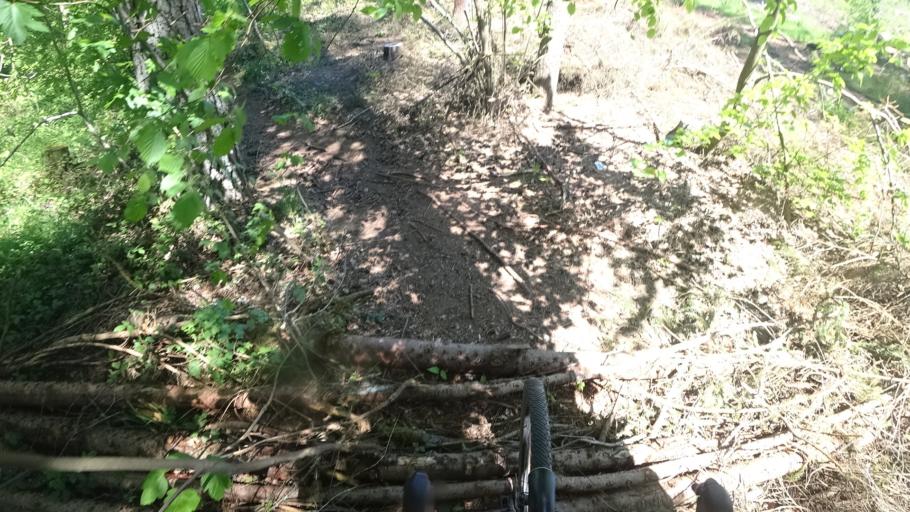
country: DE
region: Rheinland-Pfalz
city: Alsdorf
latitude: 50.7503
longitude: 7.8695
